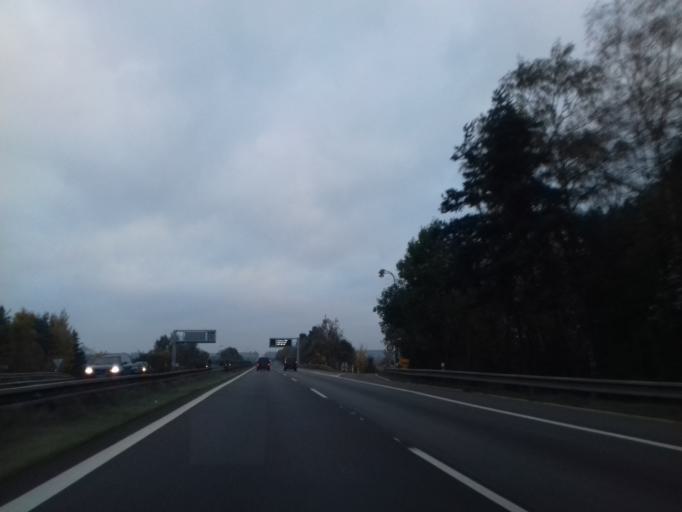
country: CZ
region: Central Bohemia
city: Zruc nad Sazavou
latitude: 49.6764
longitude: 15.1161
